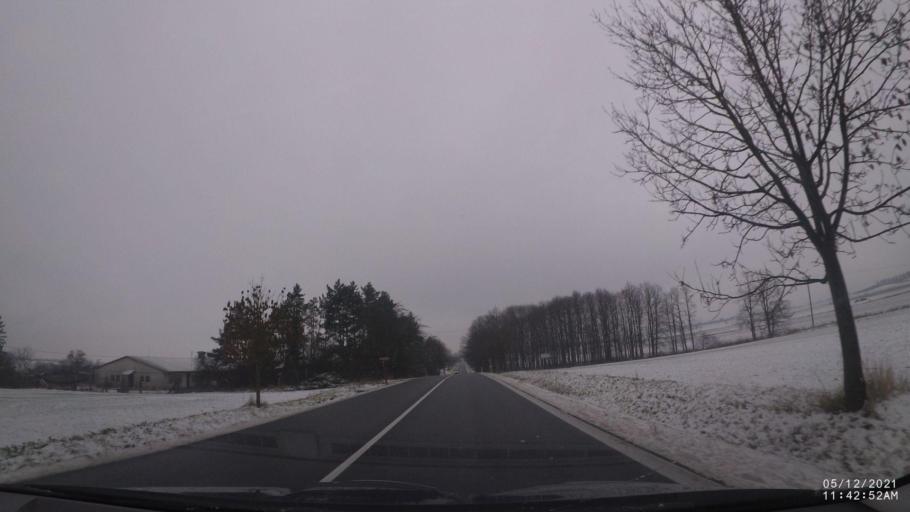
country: CZ
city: Dobruska
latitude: 50.2815
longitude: 16.1801
